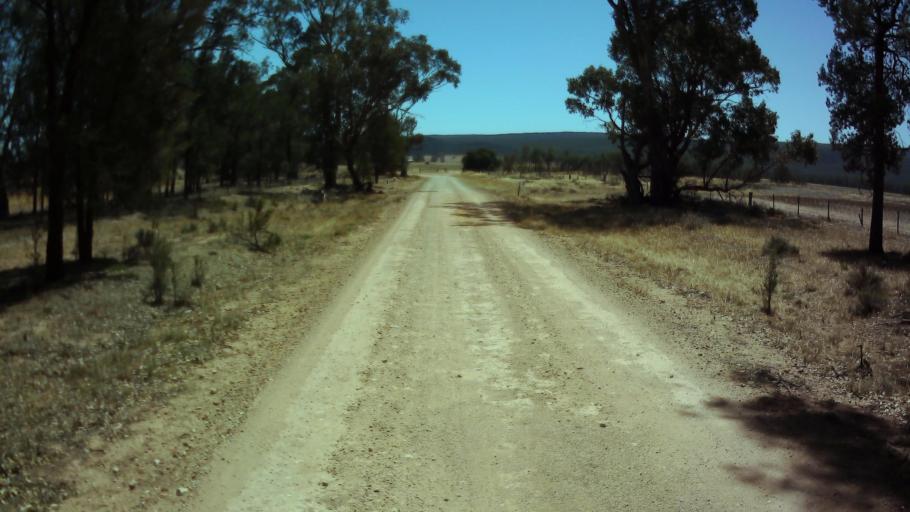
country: AU
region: New South Wales
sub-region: Weddin
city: Grenfell
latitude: -33.9942
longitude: 147.9581
